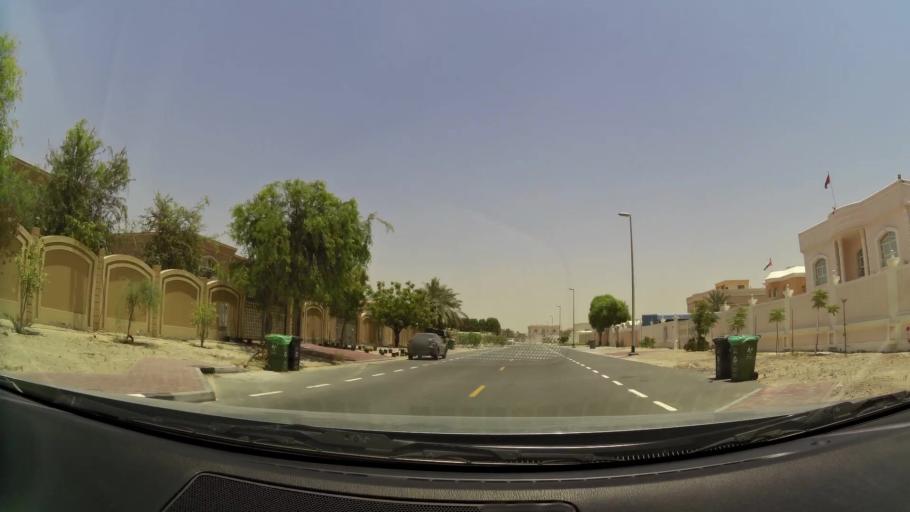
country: AE
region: Dubai
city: Dubai
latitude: 25.0986
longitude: 55.1908
